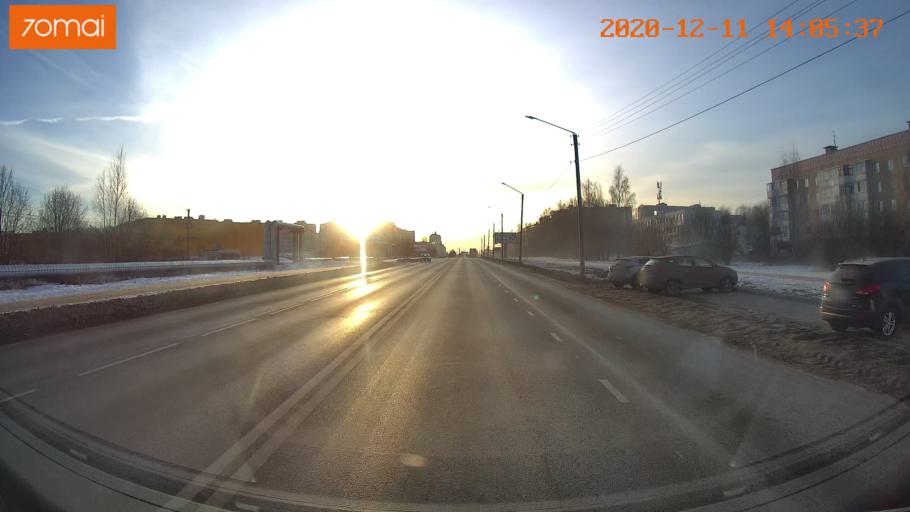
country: RU
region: Kostroma
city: Oktyabr'skiy
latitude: 57.7470
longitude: 41.0118
